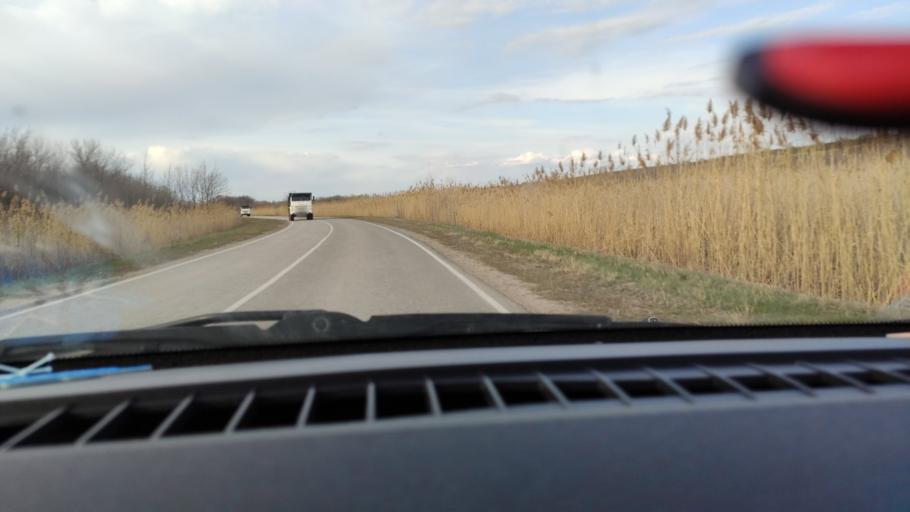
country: RU
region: Saratov
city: Privolzhskiy
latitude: 51.2649
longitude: 45.9461
